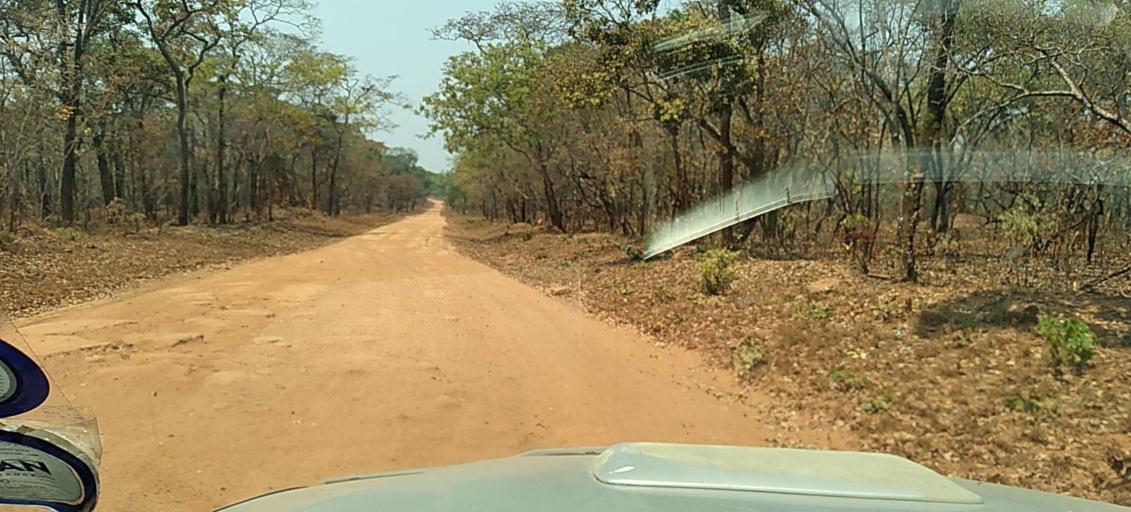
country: ZM
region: North-Western
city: Kasempa
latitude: -13.5593
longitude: 26.0792
